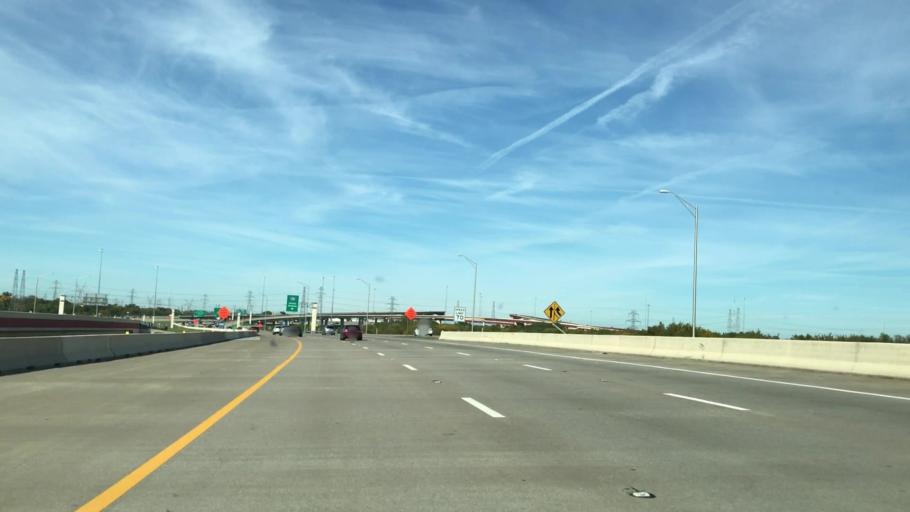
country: US
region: Texas
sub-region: Dallas County
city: Carrollton
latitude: 32.9715
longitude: -96.9324
